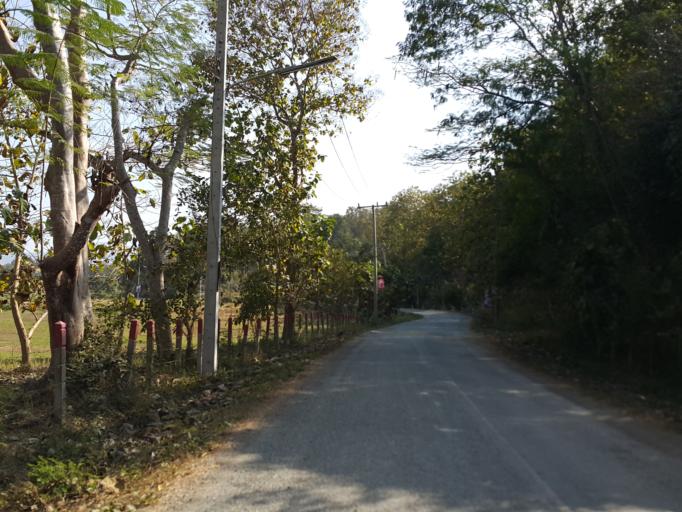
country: TH
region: Chiang Mai
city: Mae On
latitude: 18.8041
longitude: 99.2287
